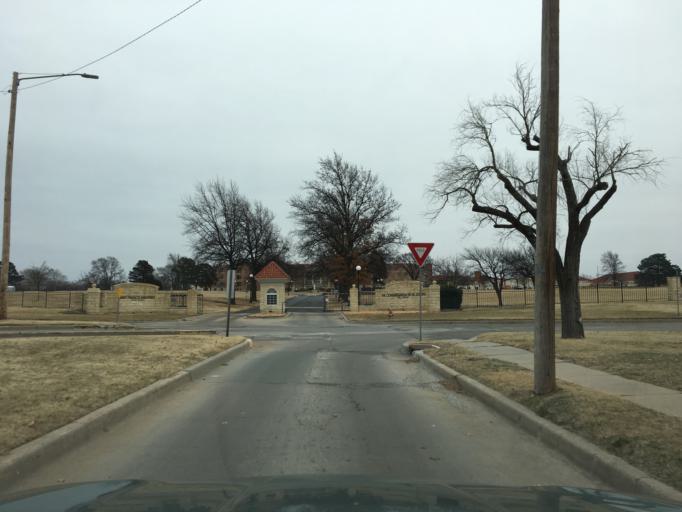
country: US
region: Kansas
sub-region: Sedgwick County
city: Wichita
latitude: 37.6719
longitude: -97.2946
